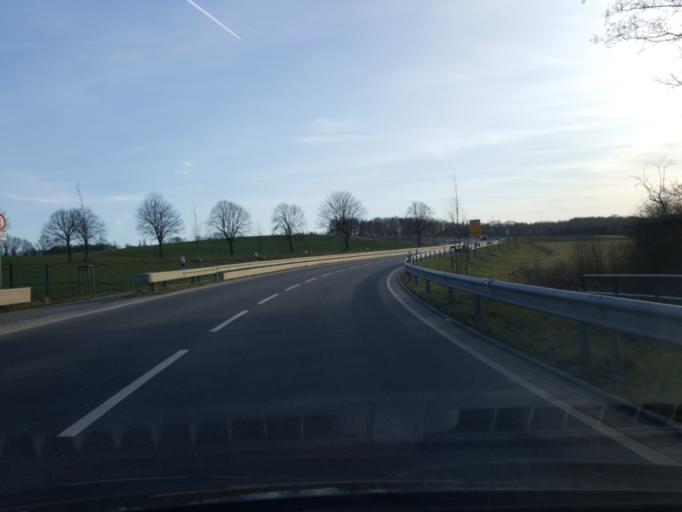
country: DE
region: Lower Saxony
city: Seevetal
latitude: 53.3861
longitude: 9.9729
